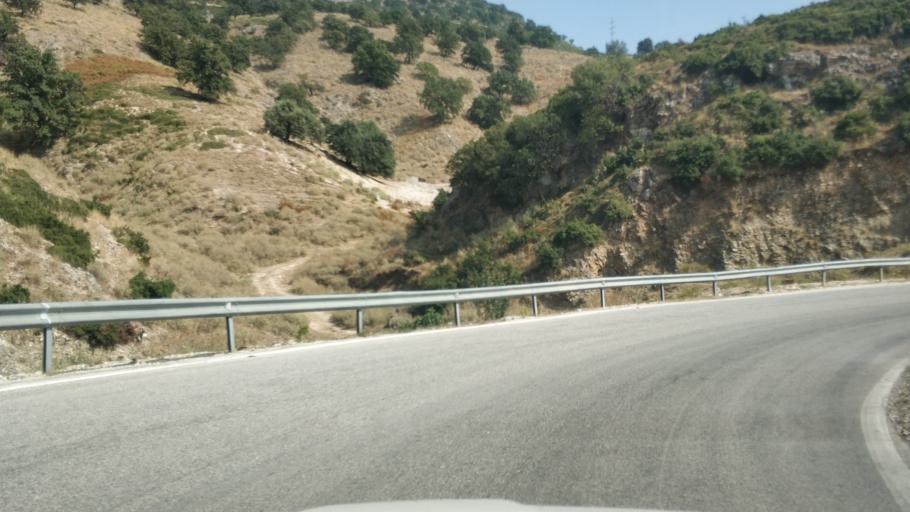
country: AL
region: Vlore
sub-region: Rrethi i Sarandes
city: Lukove
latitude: 40.0441
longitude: 19.8753
